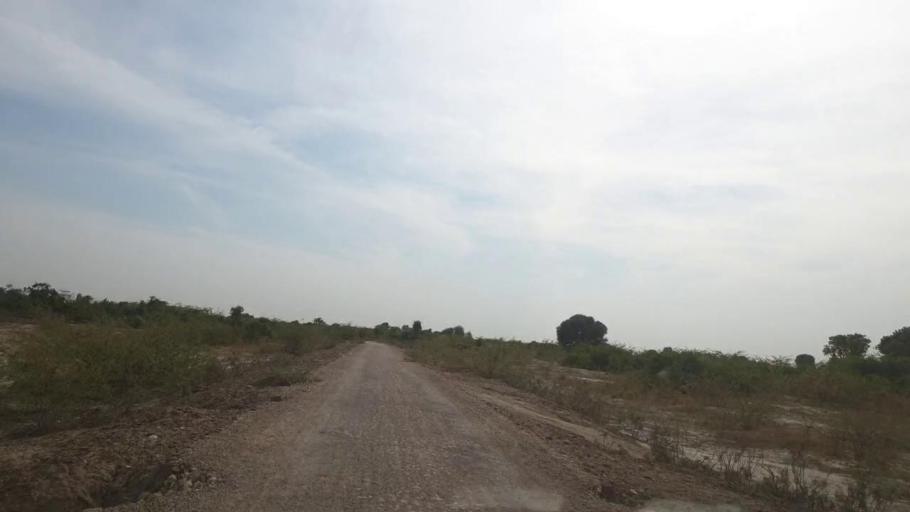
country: PK
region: Sindh
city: Nabisar
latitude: 25.0078
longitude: 69.5610
